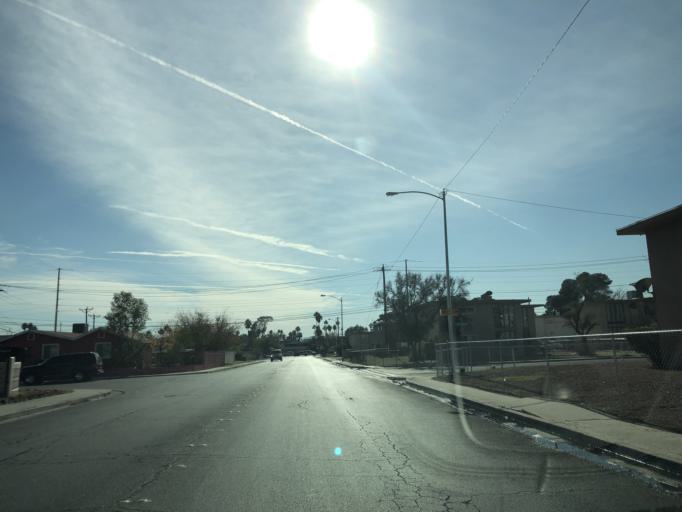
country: US
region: Nevada
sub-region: Clark County
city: Winchester
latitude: 36.1318
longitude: -115.1322
